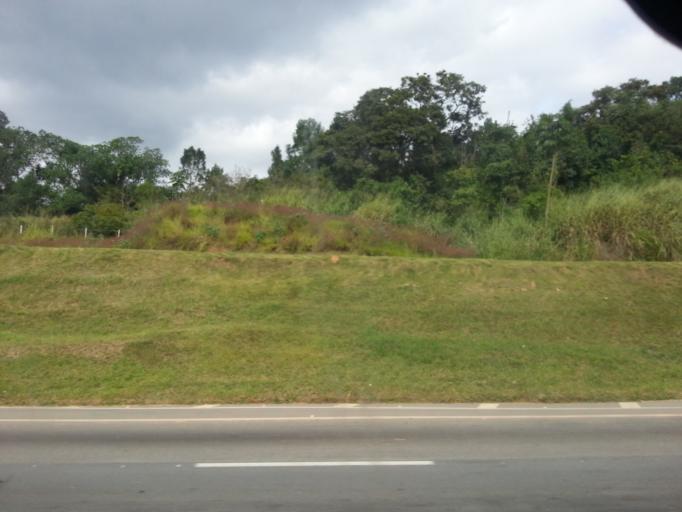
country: BR
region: Sao Paulo
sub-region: Santa Isabel
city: Santa Isabel
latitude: -23.3631
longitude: -46.2228
